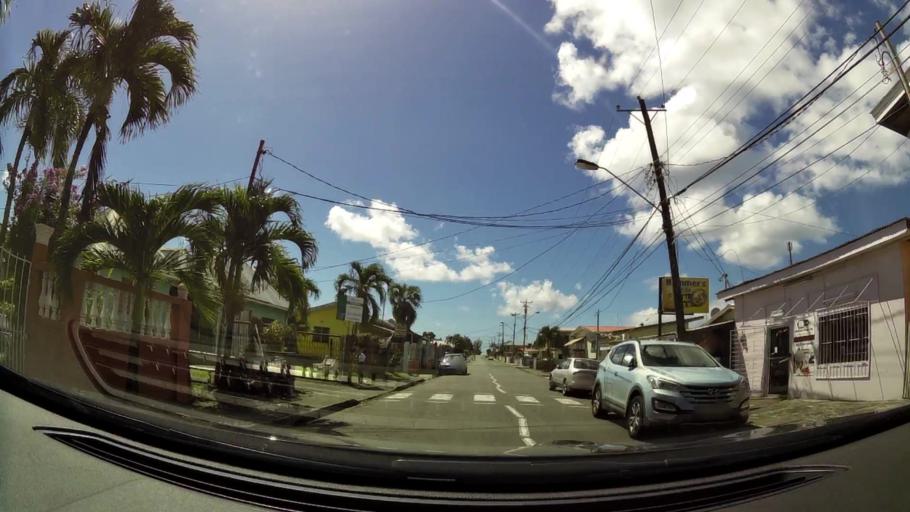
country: TT
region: Tobago
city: Scarborough
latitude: 11.2223
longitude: -60.7759
